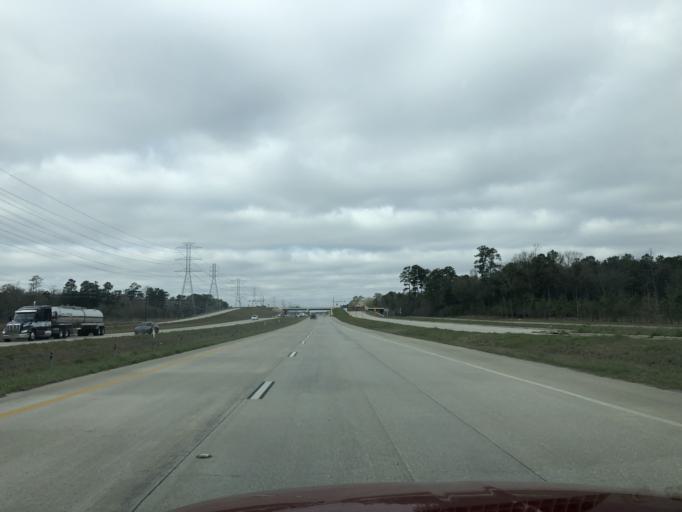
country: US
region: Texas
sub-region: Harris County
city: Spring
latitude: 30.0884
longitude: -95.4526
